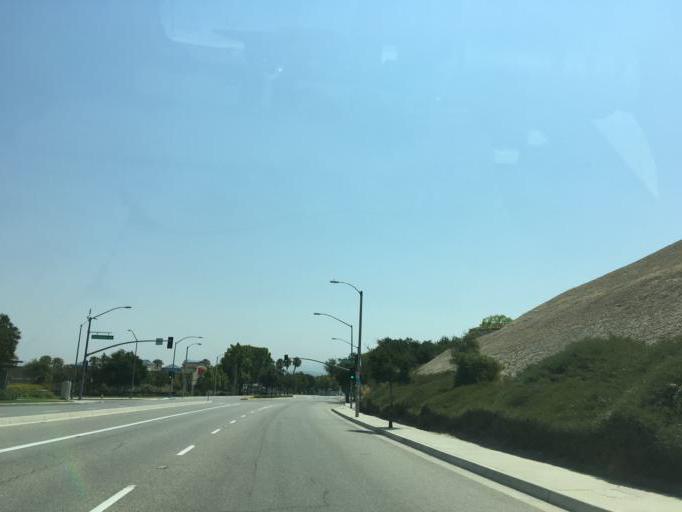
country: US
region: California
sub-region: Los Angeles County
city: Santa Clarita
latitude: 34.3817
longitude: -118.5764
